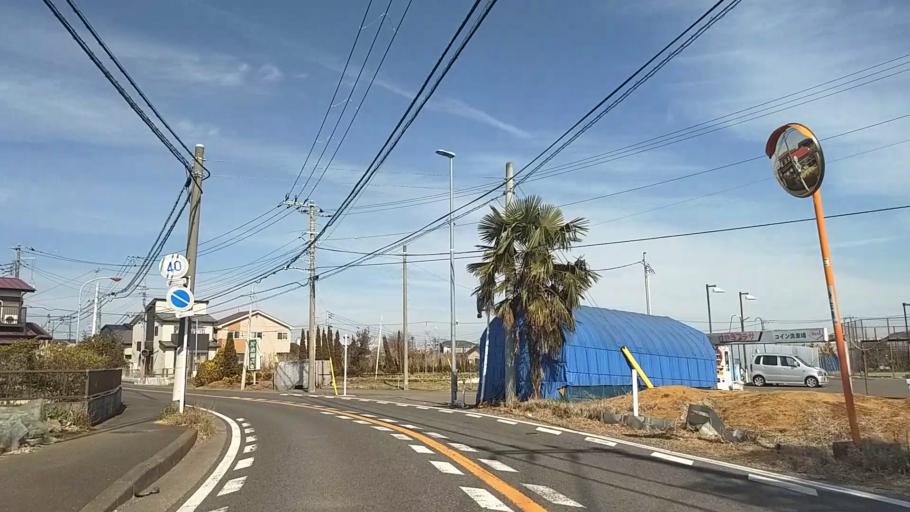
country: JP
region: Kanagawa
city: Fujisawa
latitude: 35.3800
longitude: 139.4371
